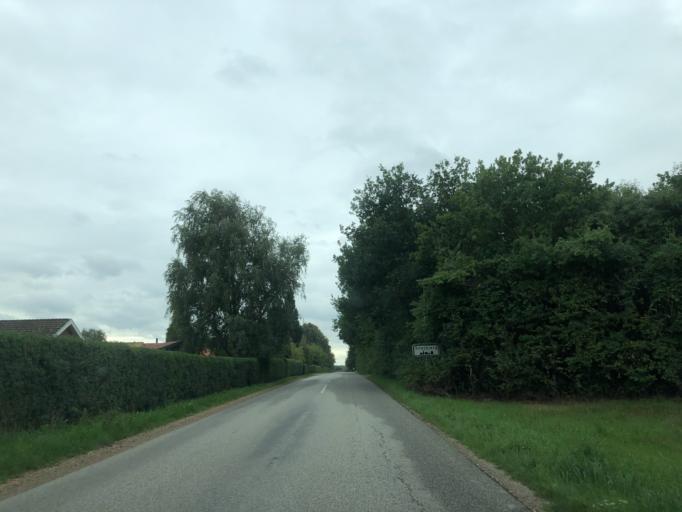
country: DK
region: Central Jutland
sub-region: Herning Kommune
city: Snejbjerg
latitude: 56.1386
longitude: 8.9070
